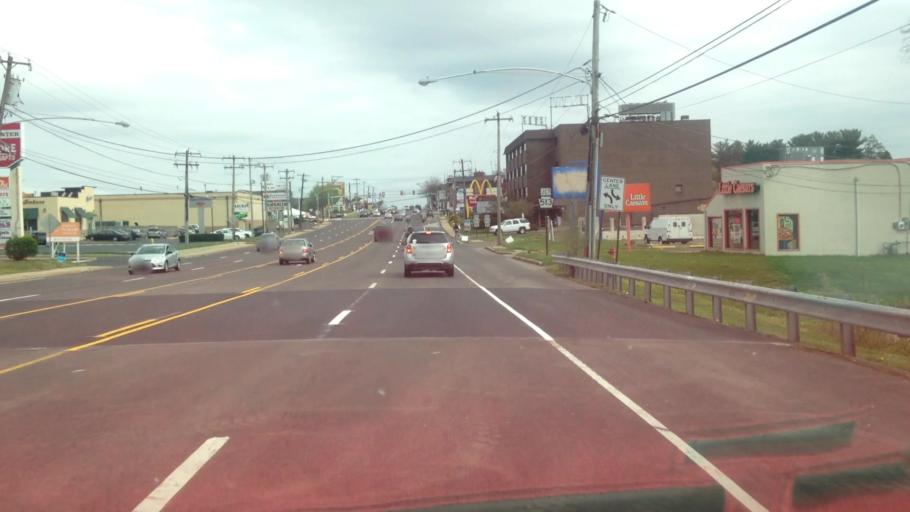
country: US
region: Pennsylvania
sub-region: Bucks County
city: Eddington
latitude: 40.0981
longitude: -74.9467
